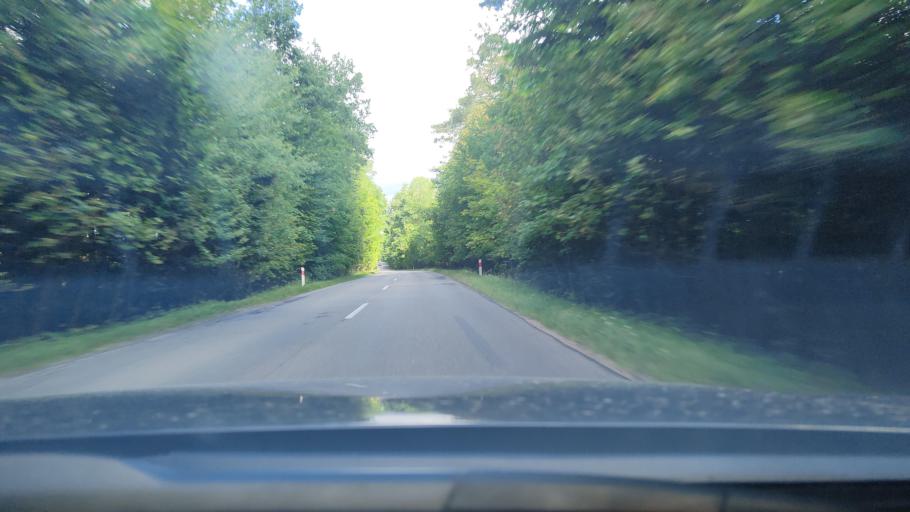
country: PL
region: Pomeranian Voivodeship
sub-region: Powiat wejherowski
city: Wejherowo
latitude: 54.6324
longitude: 18.2237
